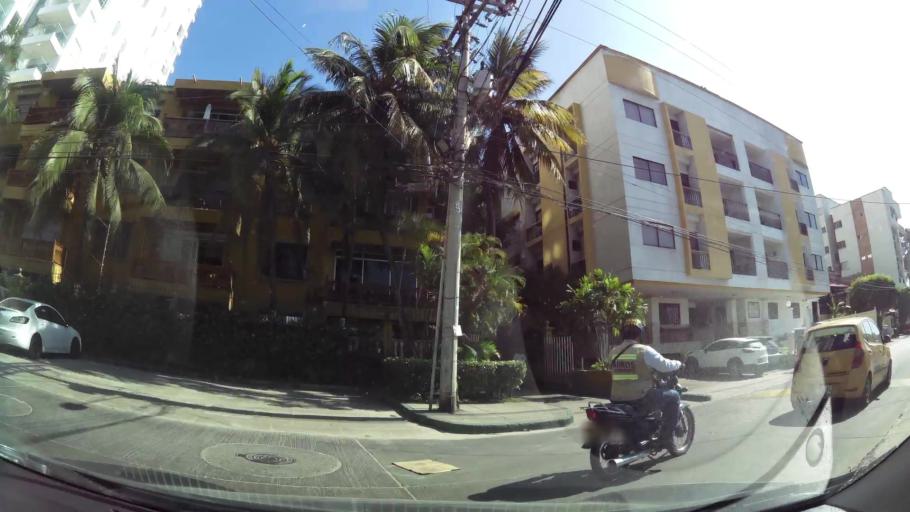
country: CO
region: Bolivar
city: Cartagena
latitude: 10.4319
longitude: -75.5429
